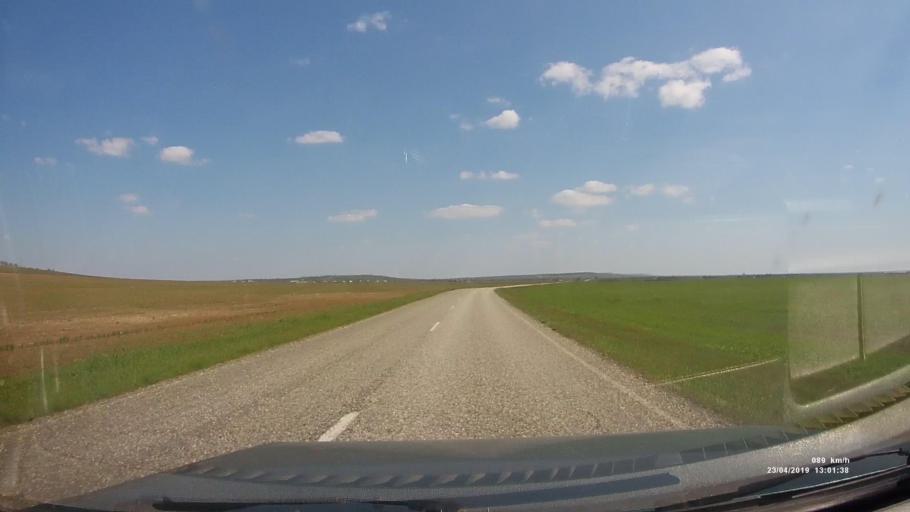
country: RU
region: Kalmykiya
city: Yashalta
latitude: 46.6038
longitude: 42.6558
